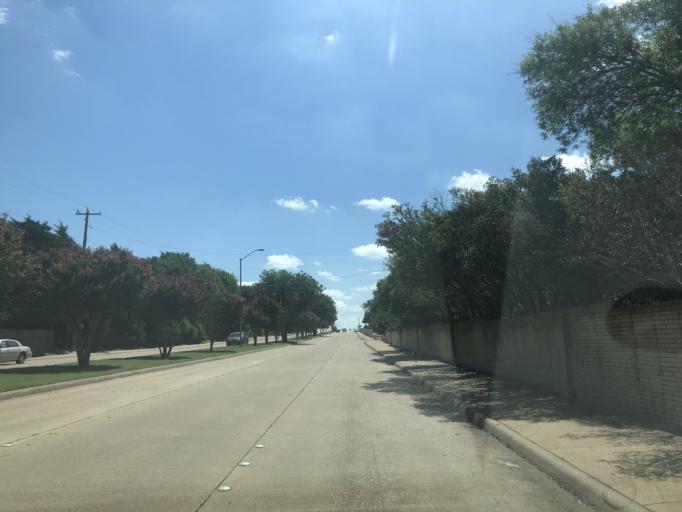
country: US
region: Texas
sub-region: Dallas County
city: Duncanville
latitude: 32.6471
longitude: -96.9383
